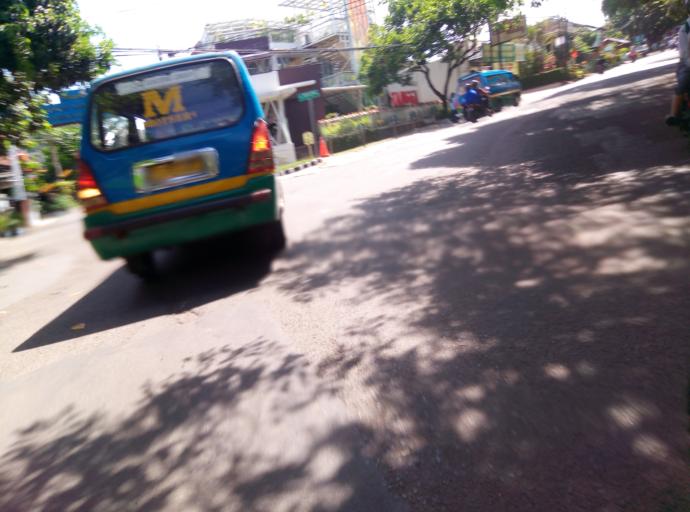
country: ID
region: West Java
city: Bandung
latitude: -6.8878
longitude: 107.6240
